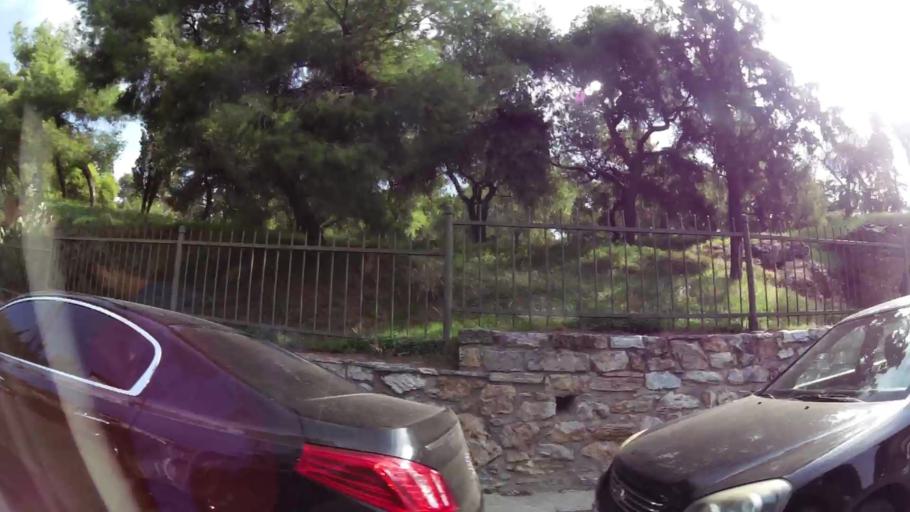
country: GR
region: Attica
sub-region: Nomarchia Athinas
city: Athens
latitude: 37.9726
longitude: 23.7167
